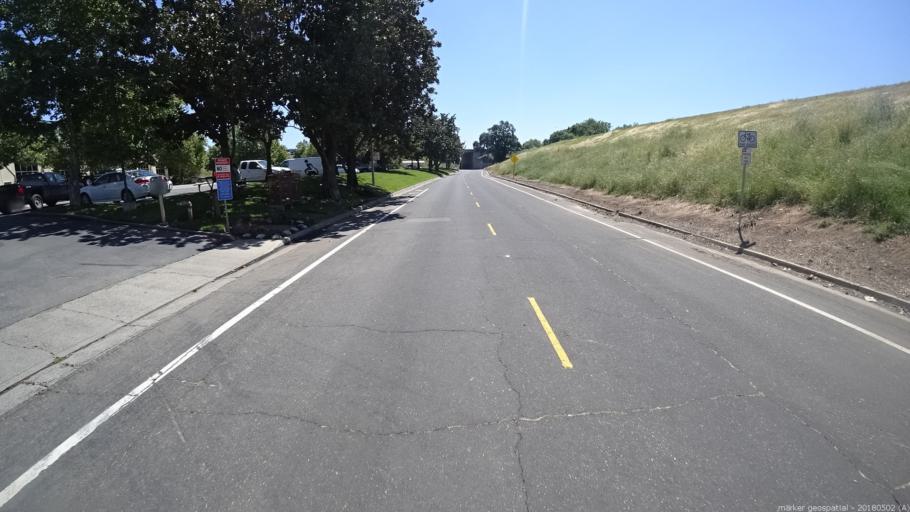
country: US
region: California
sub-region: Sacramento County
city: Sacramento
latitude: 38.5949
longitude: -121.4462
